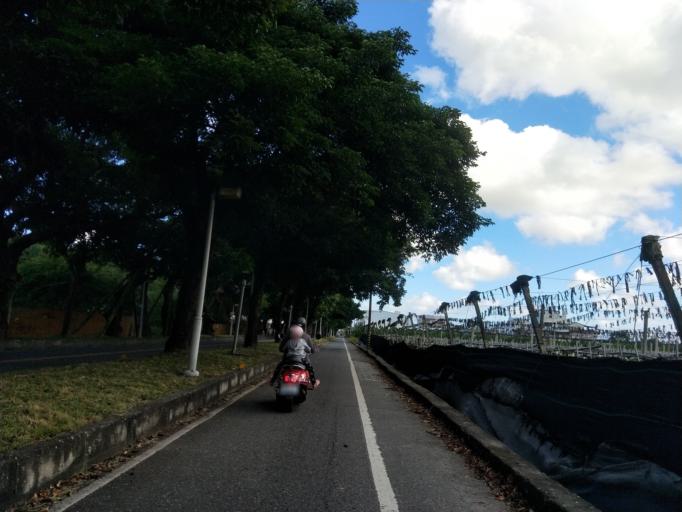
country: TW
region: Taiwan
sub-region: Taitung
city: Taitung
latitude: 22.7916
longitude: 121.1072
